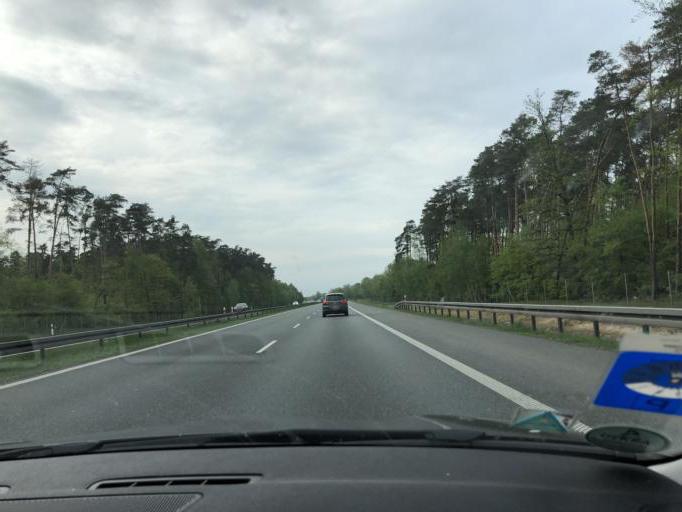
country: PL
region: Opole Voivodeship
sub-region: Powiat brzeski
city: Lewin Brzeski
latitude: 50.6985
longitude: 17.6216
